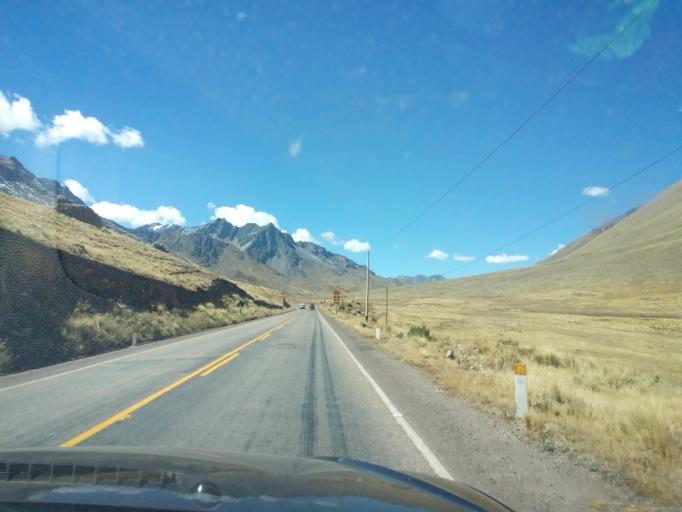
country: PE
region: Cusco
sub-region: Provincia de Canas
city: Layo
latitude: -14.4786
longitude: -71.0192
